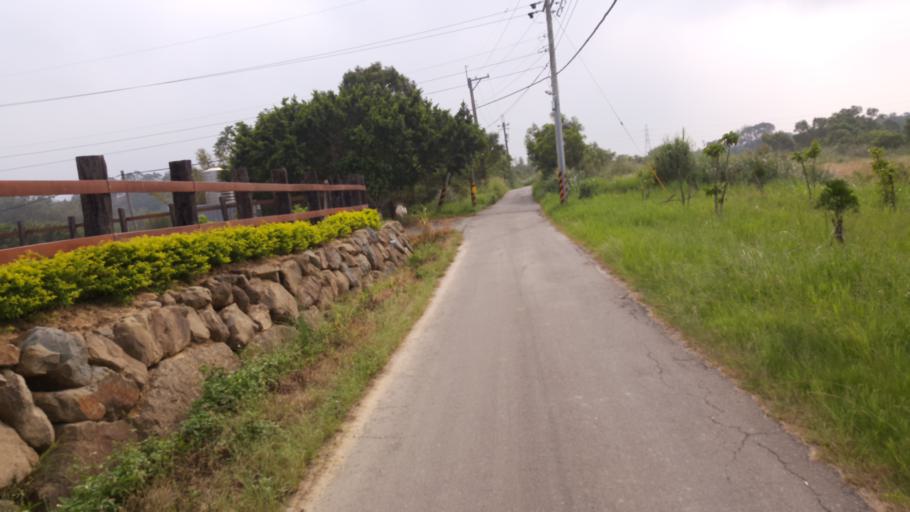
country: TW
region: Taiwan
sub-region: Hsinchu
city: Hsinchu
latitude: 24.7088
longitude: 120.9465
